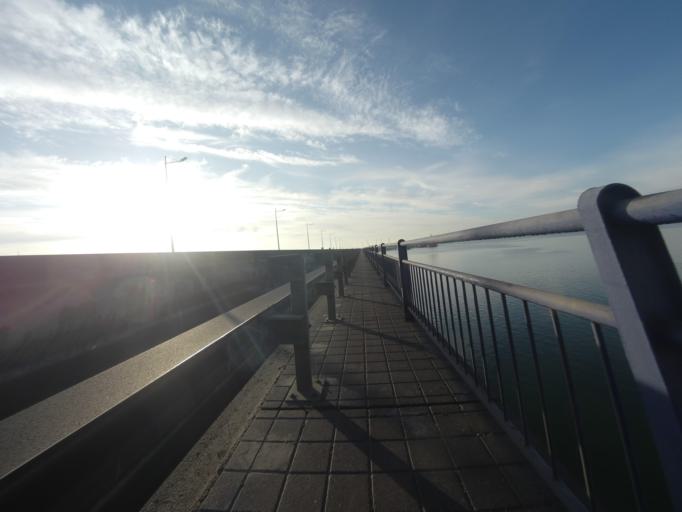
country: ES
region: Andalusia
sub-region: Provincia de Huelva
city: Punta Umbria
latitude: 37.2126
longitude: -6.9385
